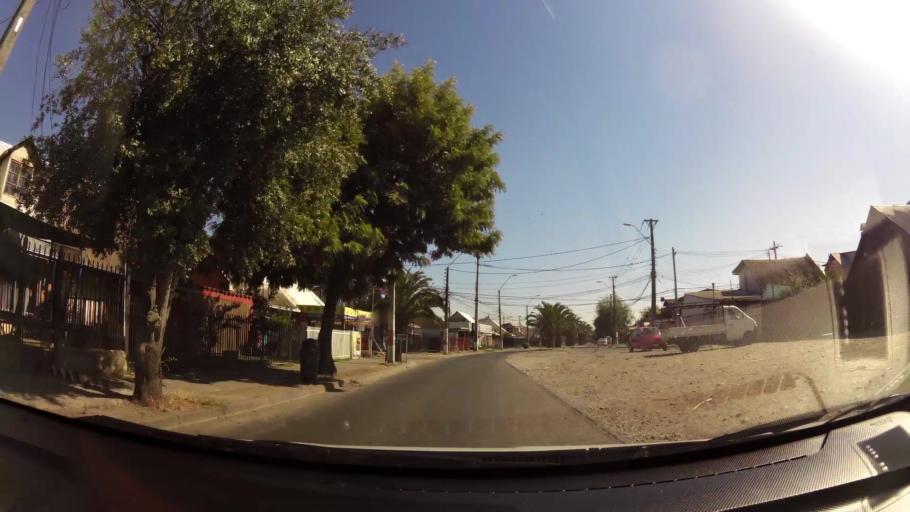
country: CL
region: Maule
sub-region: Provincia de Curico
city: Curico
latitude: -34.9802
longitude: -71.2535
